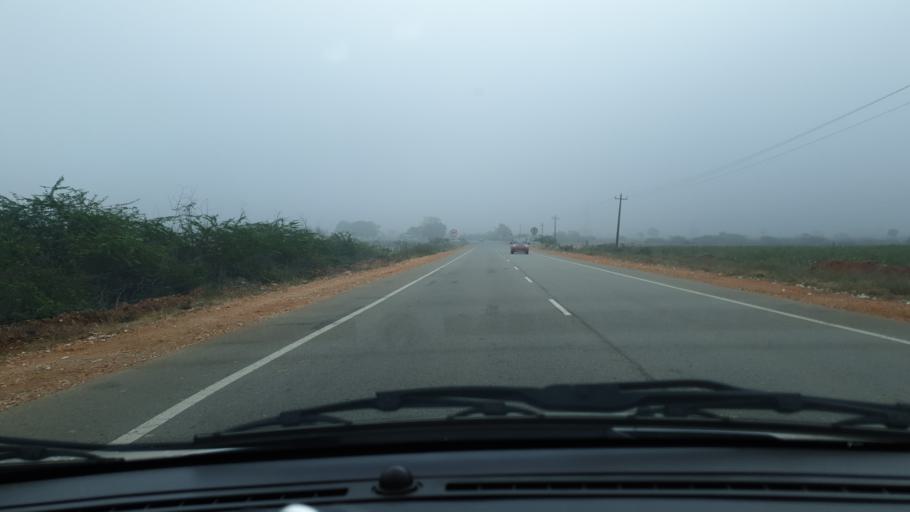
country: IN
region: Telangana
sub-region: Nalgonda
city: Devarkonda
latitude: 16.6320
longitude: 78.6073
